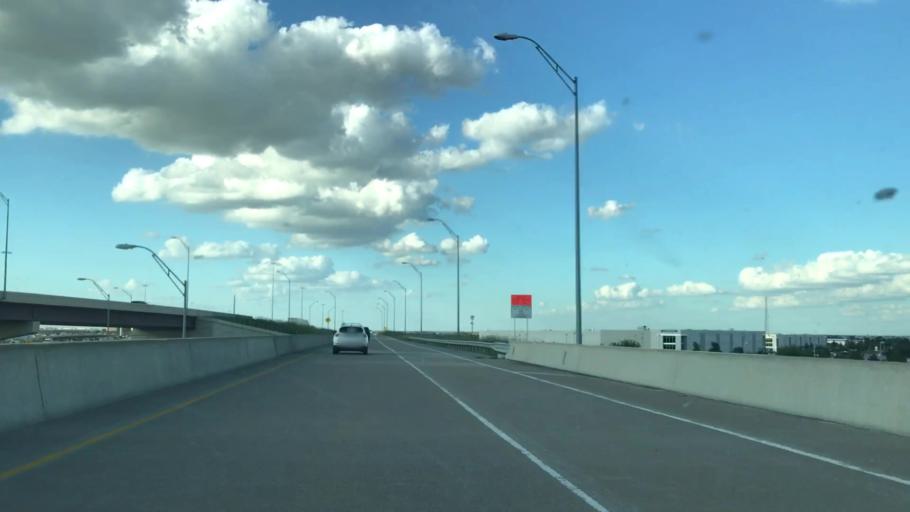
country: US
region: Texas
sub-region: Dallas County
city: Coppell
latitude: 32.9364
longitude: -97.0391
